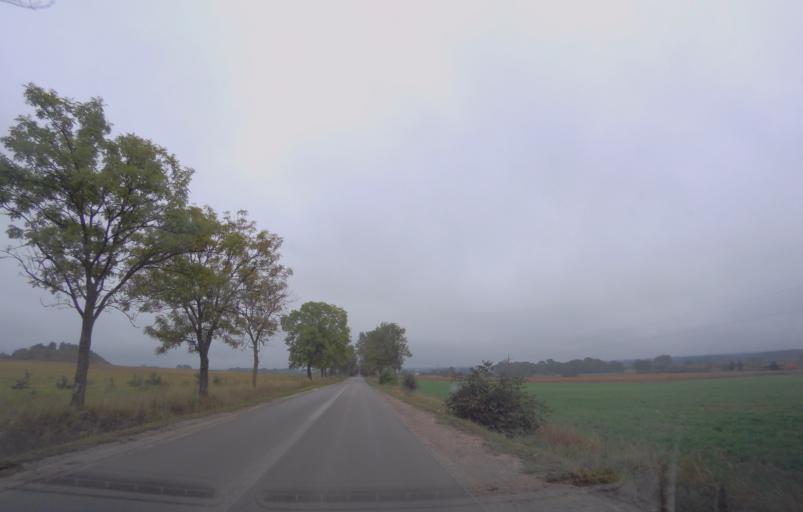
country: PL
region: Lublin Voivodeship
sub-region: Powiat chelmski
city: Sawin
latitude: 51.2138
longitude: 23.4360
